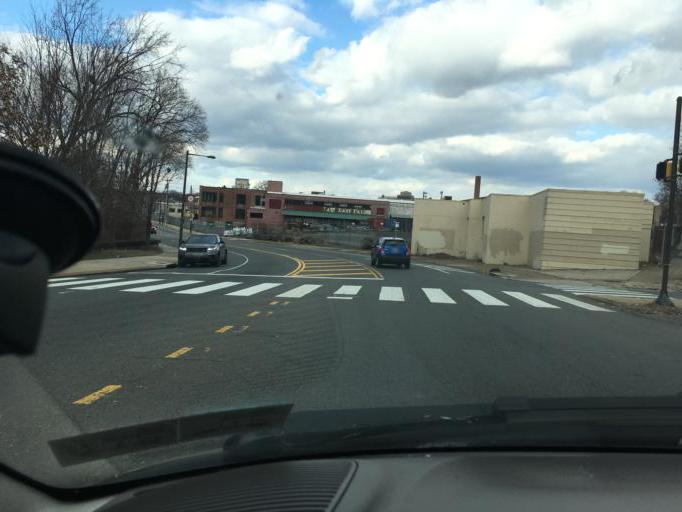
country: US
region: Pennsylvania
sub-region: Montgomery County
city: Bala-Cynwyd
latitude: 40.0006
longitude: -75.1868
